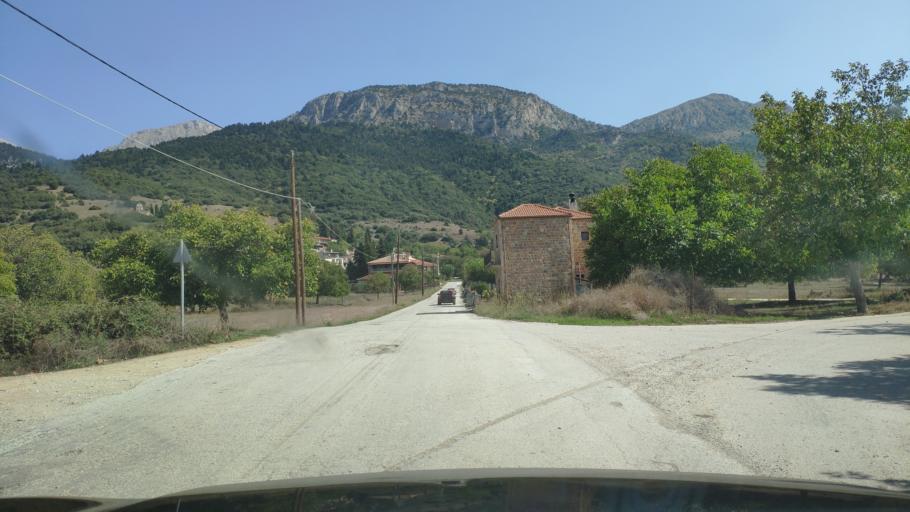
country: GR
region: West Greece
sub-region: Nomos Achaias
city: Aiyira
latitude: 37.9085
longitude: 22.3286
